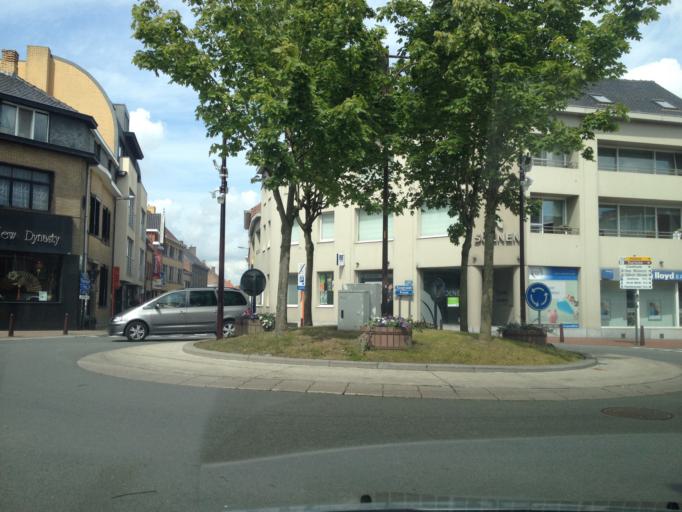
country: BE
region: Flanders
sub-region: Provincie West-Vlaanderen
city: Poperinge
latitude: 50.8546
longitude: 2.7226
